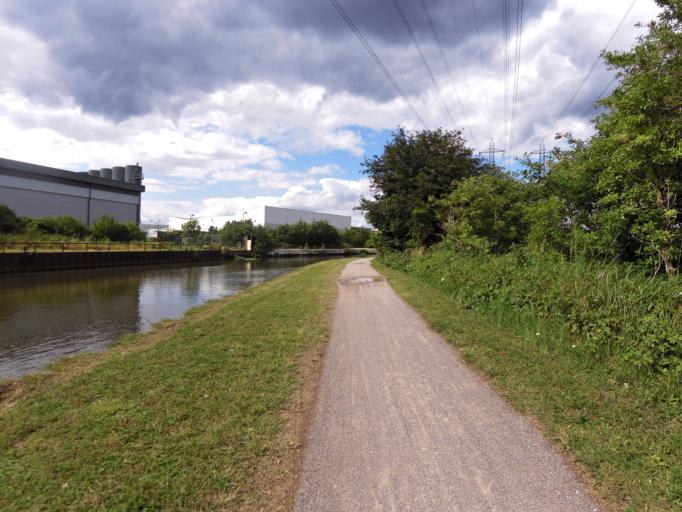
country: GB
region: England
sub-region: Essex
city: Waltham Abbey
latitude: 51.6538
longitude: -0.0203
